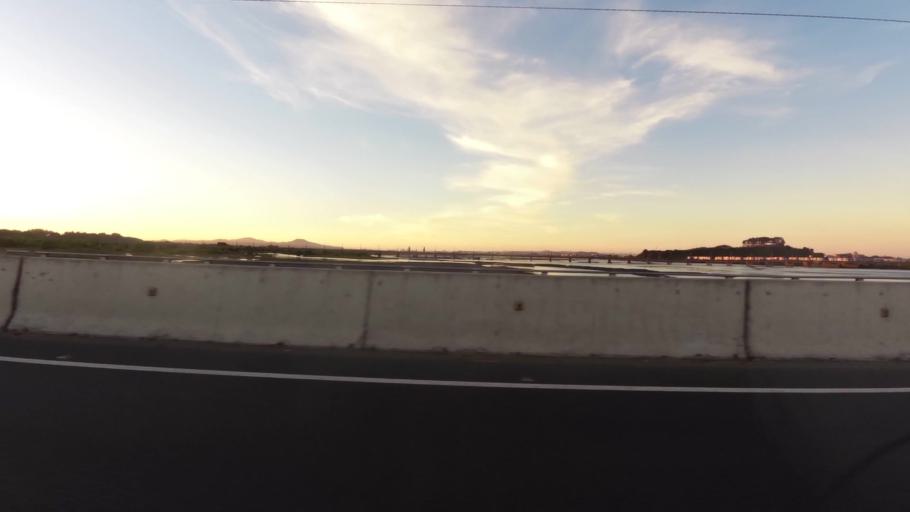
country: CL
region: Biobio
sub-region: Provincia de Concepcion
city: Concepcion
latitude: -36.8407
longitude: -73.0713
